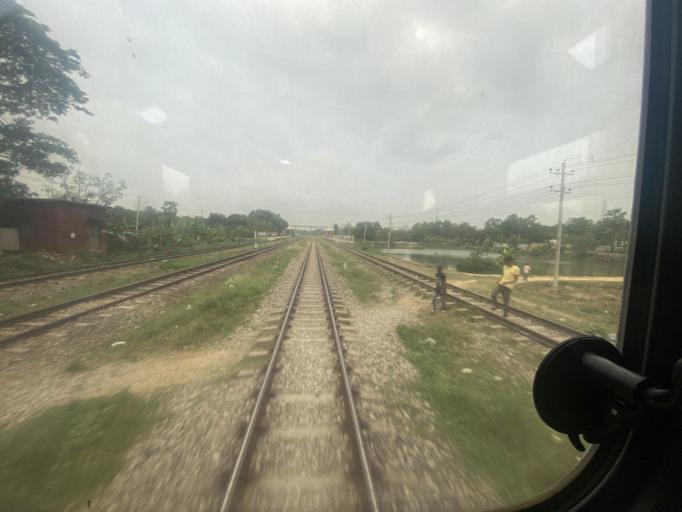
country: BD
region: Dhaka
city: Tungi
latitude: 23.9365
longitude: 90.4783
